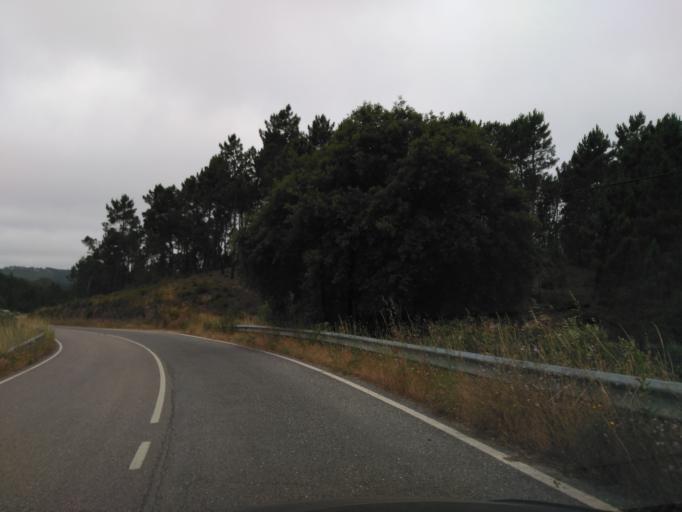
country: PT
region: Santarem
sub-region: Abrantes
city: Alferrarede
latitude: 39.5741
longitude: -8.1144
